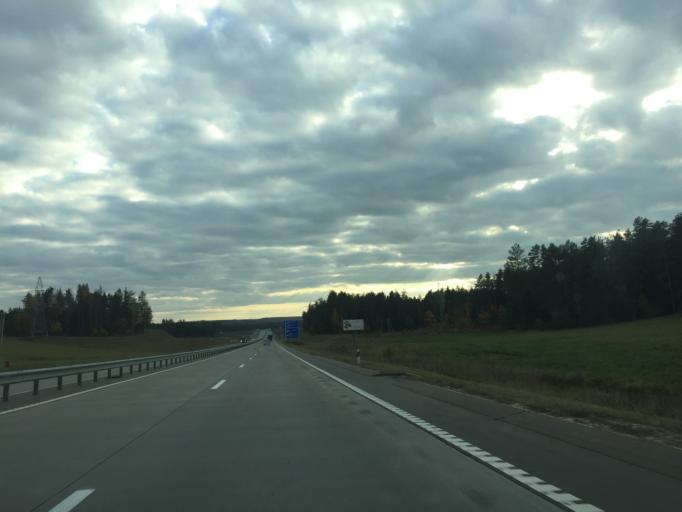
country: BY
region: Minsk
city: Rakaw
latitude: 53.9760
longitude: 27.0960
